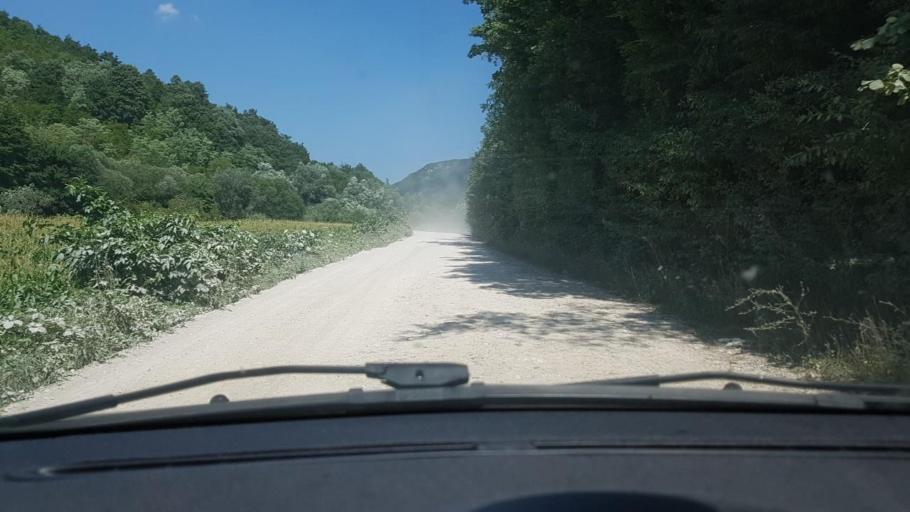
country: BA
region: Federation of Bosnia and Herzegovina
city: Orasac
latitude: 44.5084
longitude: 16.1276
